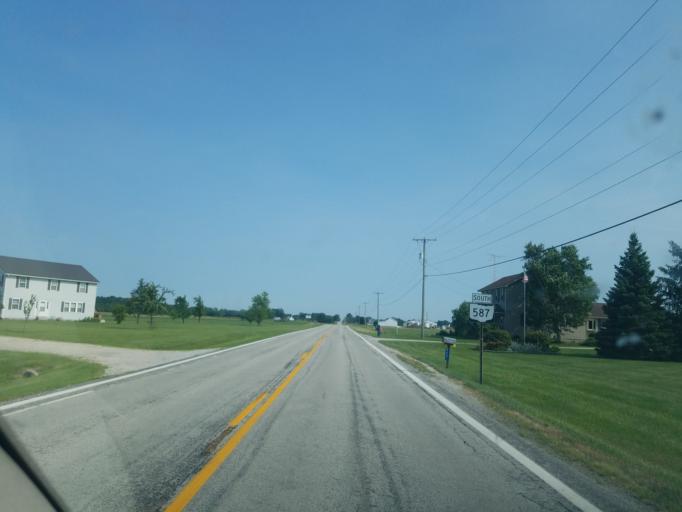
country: US
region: Ohio
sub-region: Wyandot County
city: Carey
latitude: 41.0434
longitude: -83.3111
